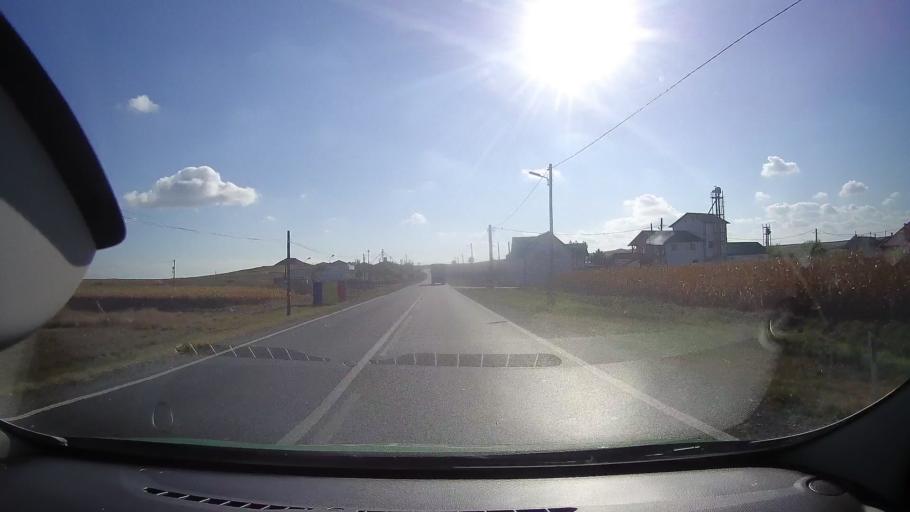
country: RO
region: Tulcea
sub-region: Comuna Baia
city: Baia
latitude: 44.7204
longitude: 28.6795
